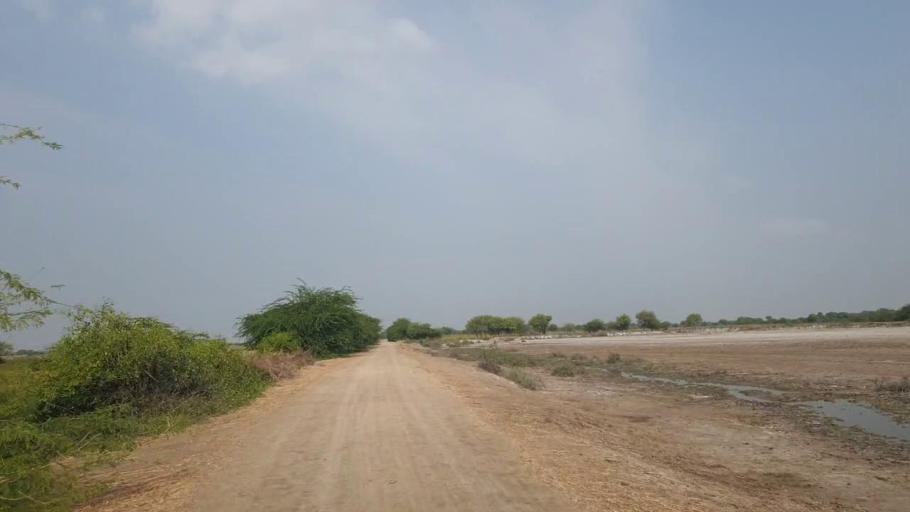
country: PK
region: Sindh
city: Badin
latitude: 24.5550
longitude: 68.7313
